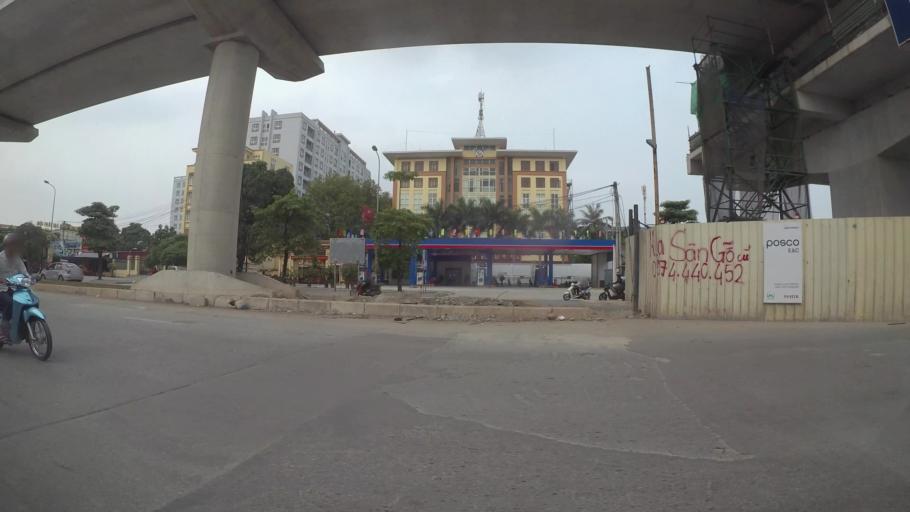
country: VN
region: Ha Noi
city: Cau Dien
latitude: 21.0440
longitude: 105.7547
